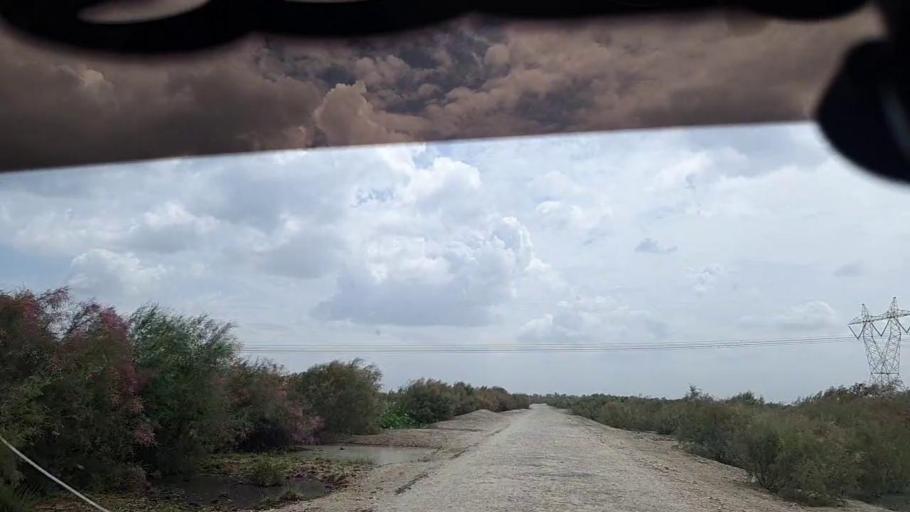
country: PK
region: Sindh
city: Ghauspur
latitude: 28.0664
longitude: 68.9388
